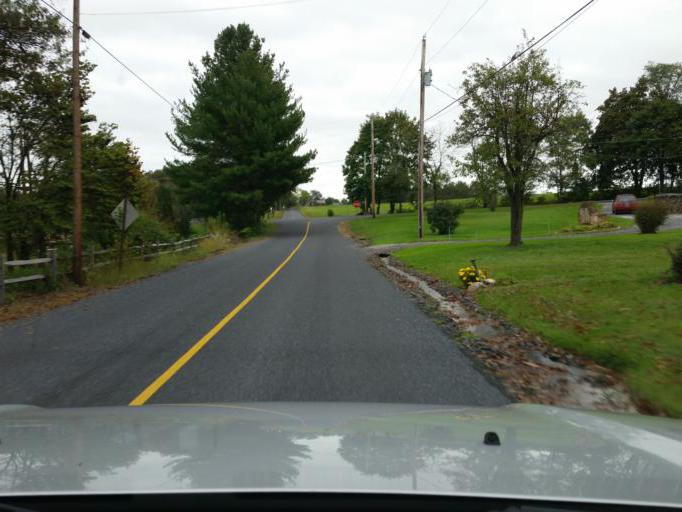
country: US
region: Pennsylvania
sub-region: Adams County
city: Biglerville
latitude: 39.9242
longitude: -77.2253
